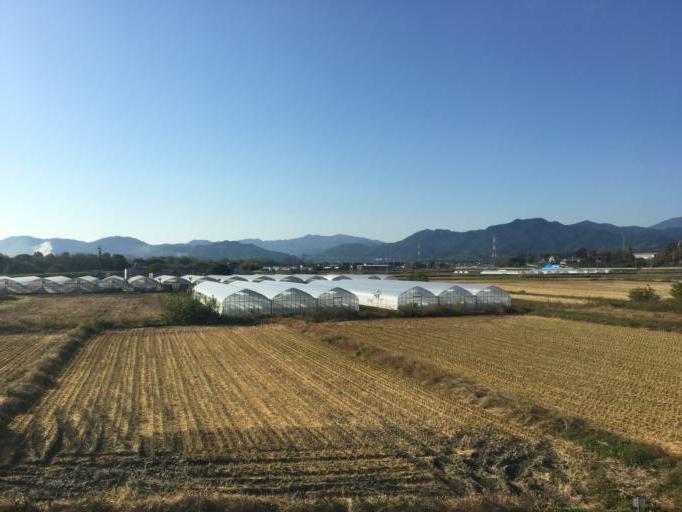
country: JP
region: Gunma
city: Fujioka
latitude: 36.2266
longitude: 139.0842
